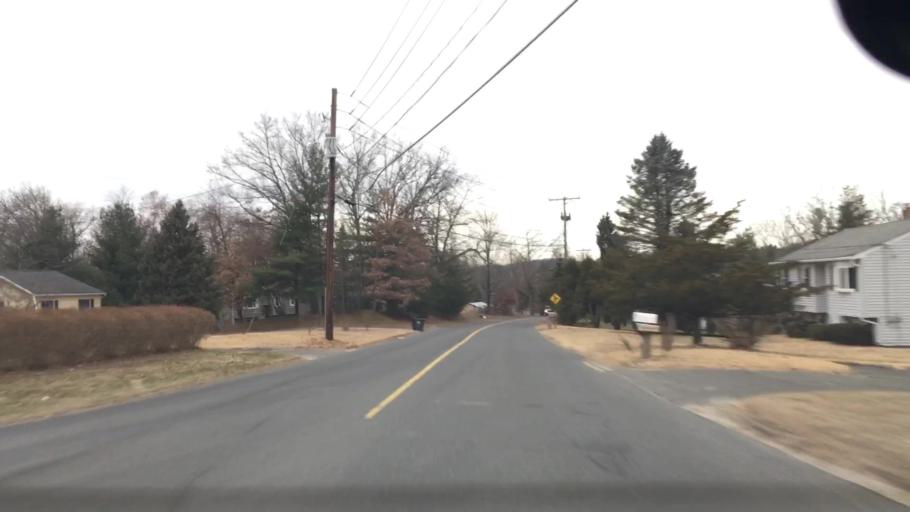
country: US
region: Connecticut
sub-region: Fairfield County
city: Bethel
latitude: 41.3963
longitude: -73.4034
